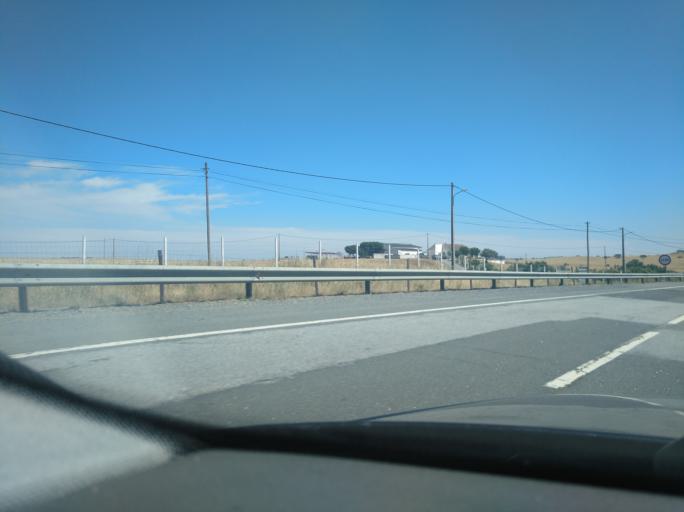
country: PT
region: Beja
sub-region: Castro Verde
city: Castro Verde
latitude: 37.6880
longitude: -8.0842
